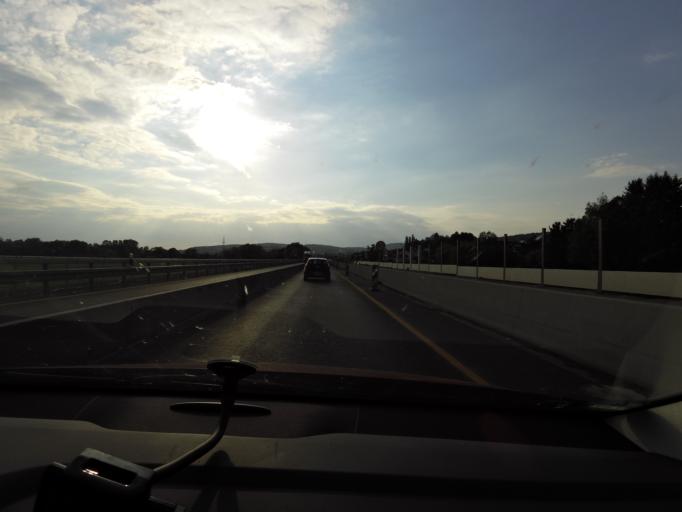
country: DE
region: Hesse
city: Oberbiel
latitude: 50.5503
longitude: 8.4241
